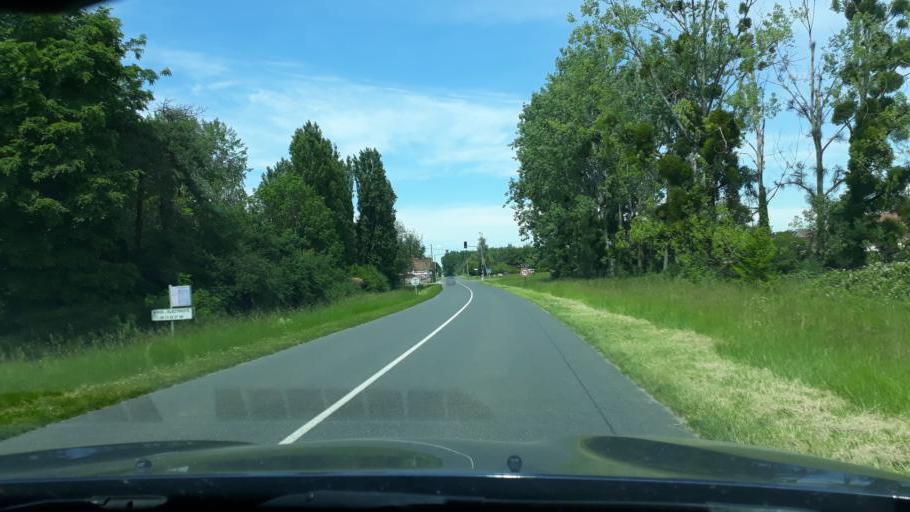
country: FR
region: Centre
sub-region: Departement du Loiret
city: Boynes
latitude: 48.0645
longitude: 2.2877
